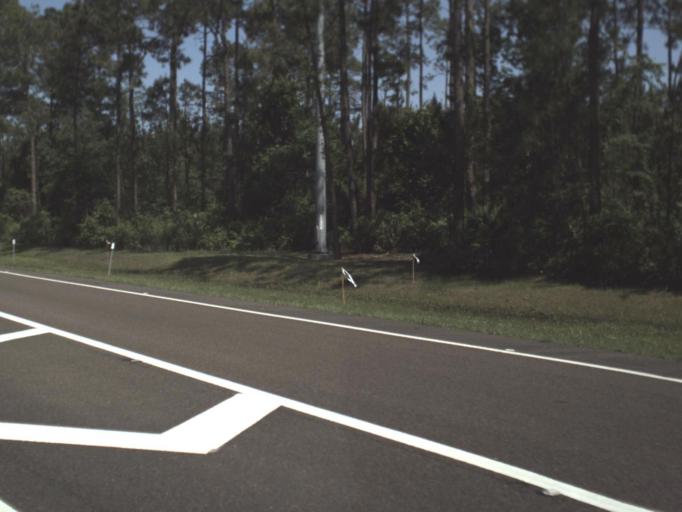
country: US
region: Florida
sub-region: Duval County
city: Baldwin
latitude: 30.3054
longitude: -81.8883
